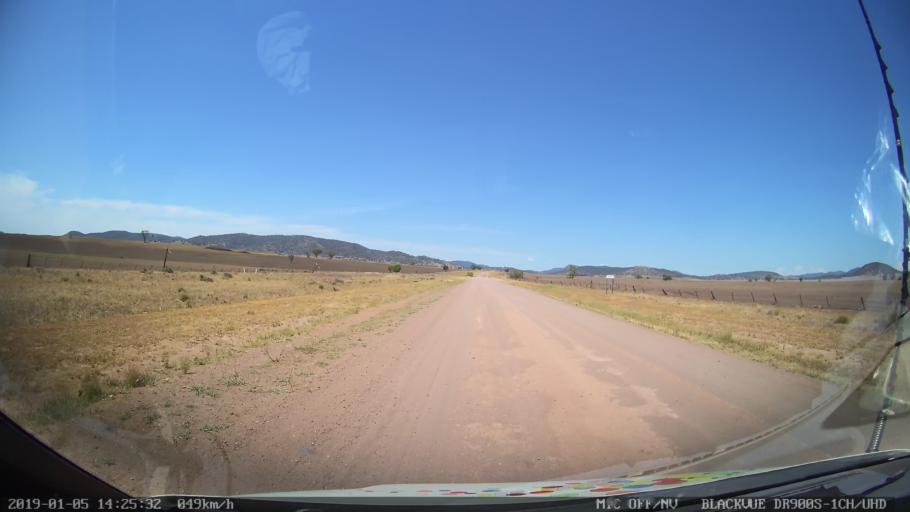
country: AU
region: New South Wales
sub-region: Liverpool Plains
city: Quirindi
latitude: -31.2404
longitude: 150.5501
